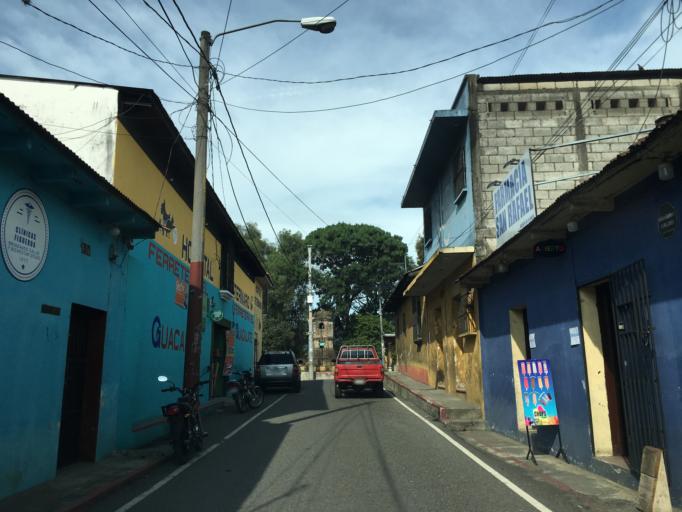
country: GT
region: Sacatepequez
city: Ciudad Vieja
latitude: 14.5256
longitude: -90.7630
